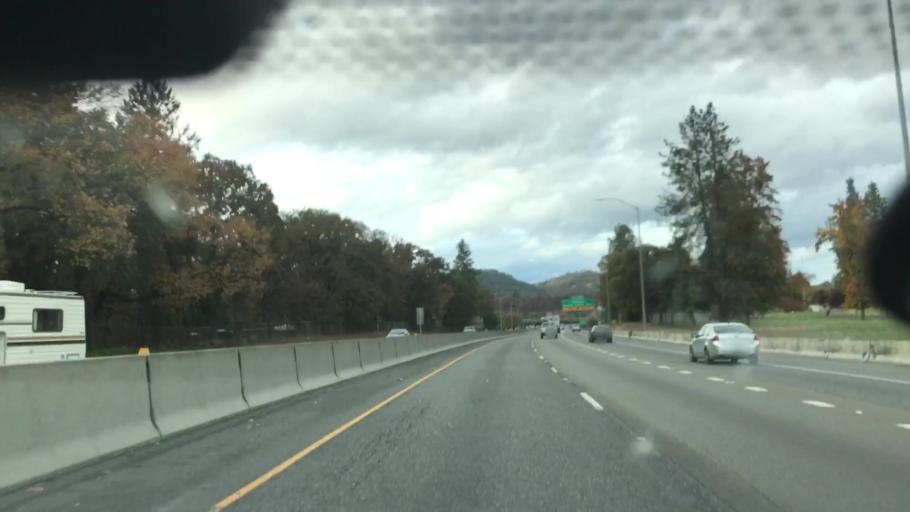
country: US
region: Oregon
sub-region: Douglas County
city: Roseburg
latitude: 43.2207
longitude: -123.3586
